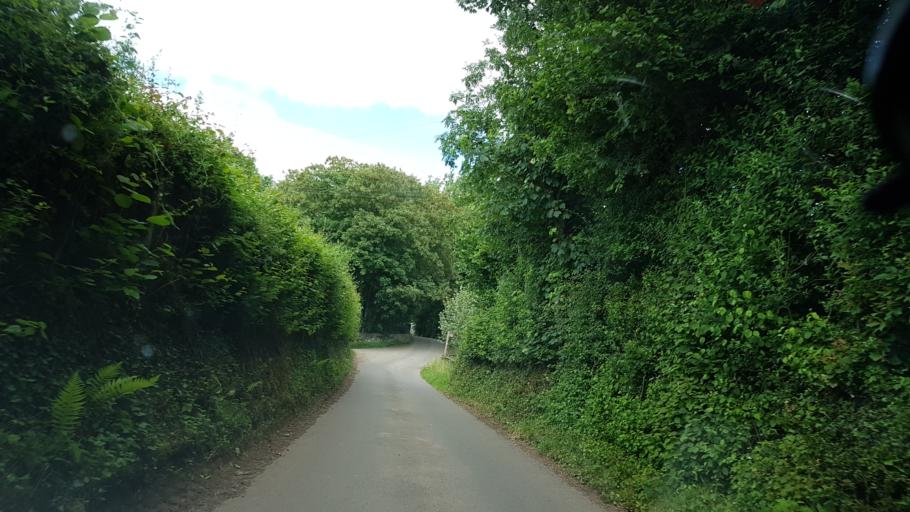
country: GB
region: Wales
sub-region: Monmouthshire
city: Llanarth
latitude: 51.8261
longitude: -2.8729
